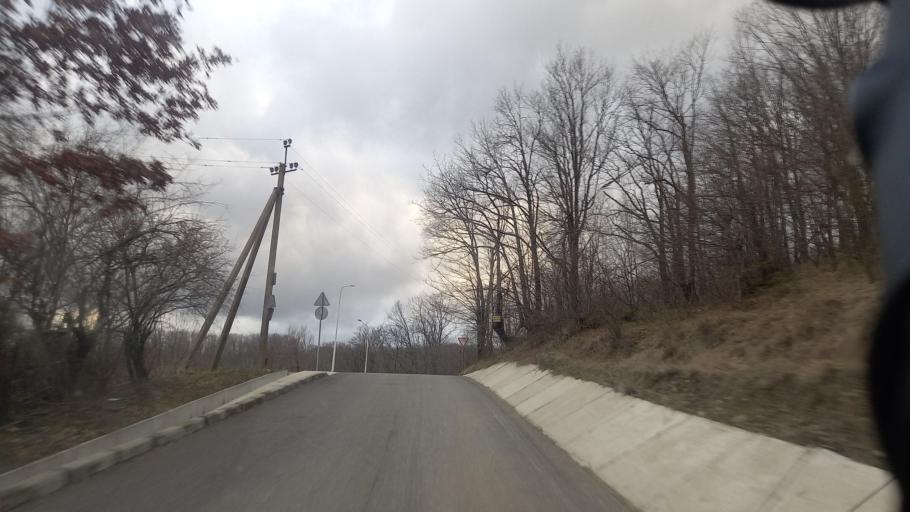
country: RU
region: Krasnodarskiy
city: Lermontovo
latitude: 44.4305
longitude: 38.7848
